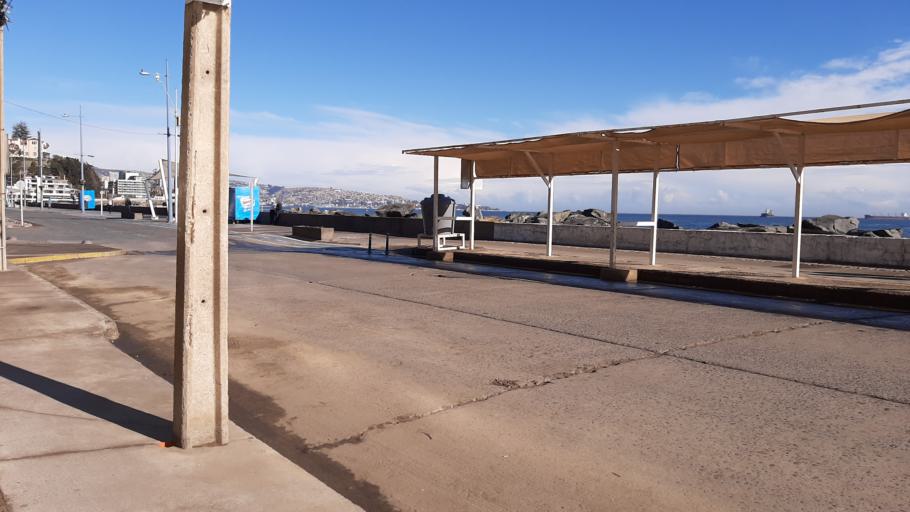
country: CL
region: Valparaiso
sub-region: Provincia de Valparaiso
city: Vina del Mar
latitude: -33.0169
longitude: -71.5592
